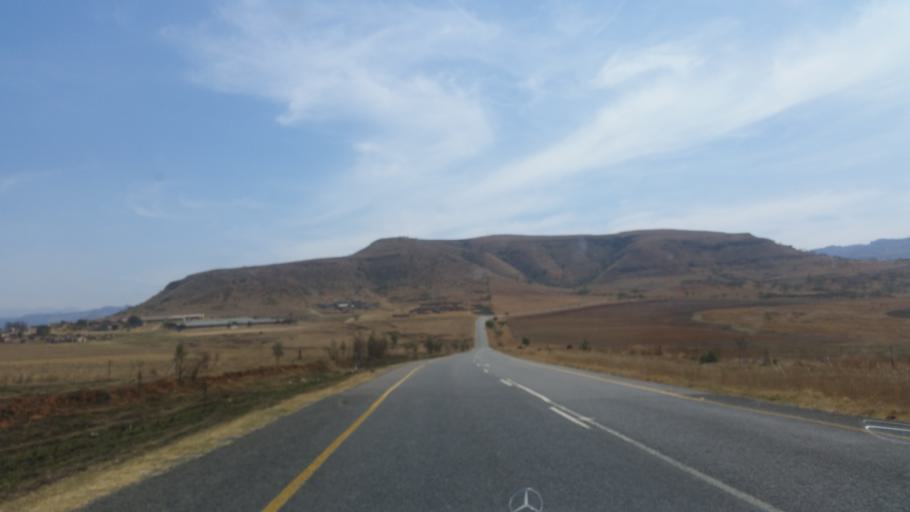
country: ZA
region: KwaZulu-Natal
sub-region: uThukela District Municipality
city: Bergville
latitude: -28.6233
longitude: 29.0919
